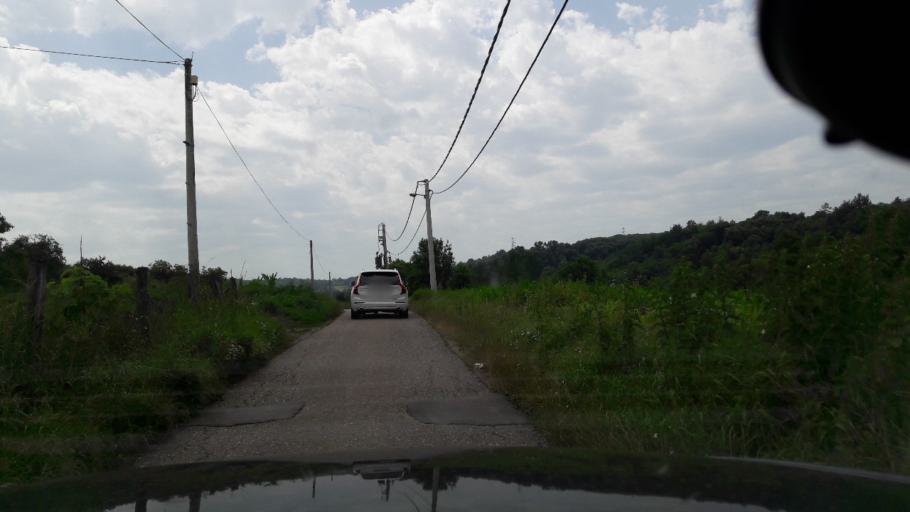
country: RS
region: Central Serbia
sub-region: Belgrade
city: Sopot
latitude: 44.6329
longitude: 20.5931
